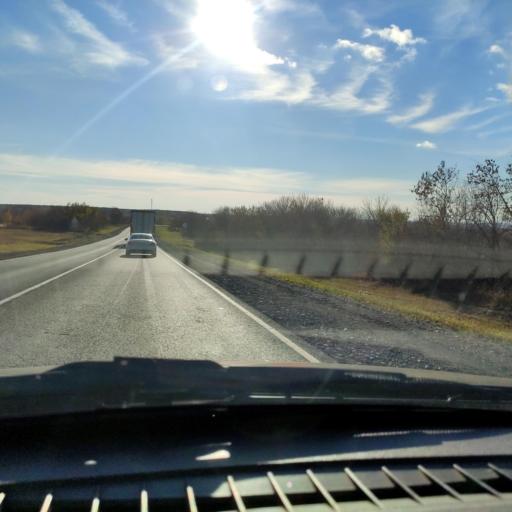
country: RU
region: Samara
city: Zhigulevsk
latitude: 53.3057
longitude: 49.3502
